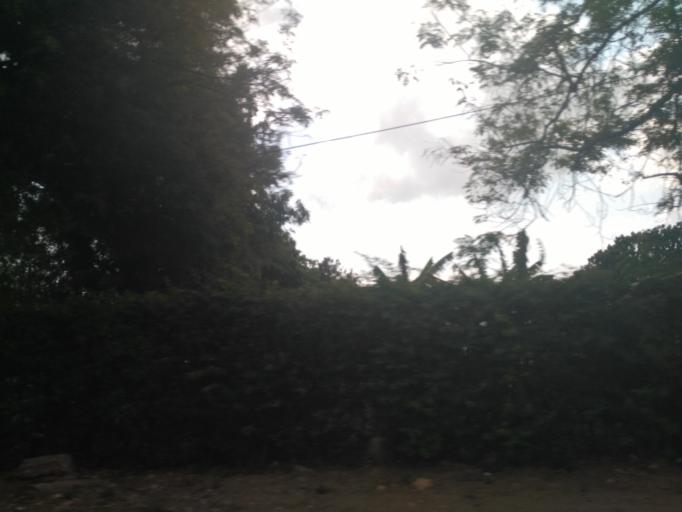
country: TZ
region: Dar es Salaam
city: Dar es Salaam
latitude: -6.8009
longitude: 39.2874
